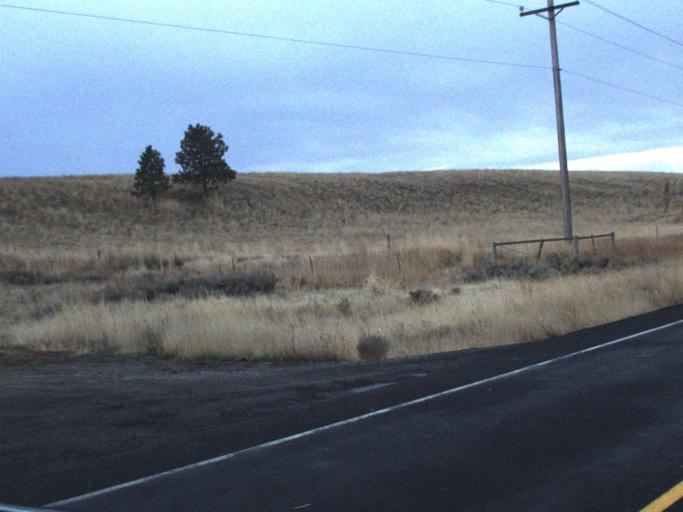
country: US
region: Washington
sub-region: Lincoln County
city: Davenport
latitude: 47.7776
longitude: -118.1736
